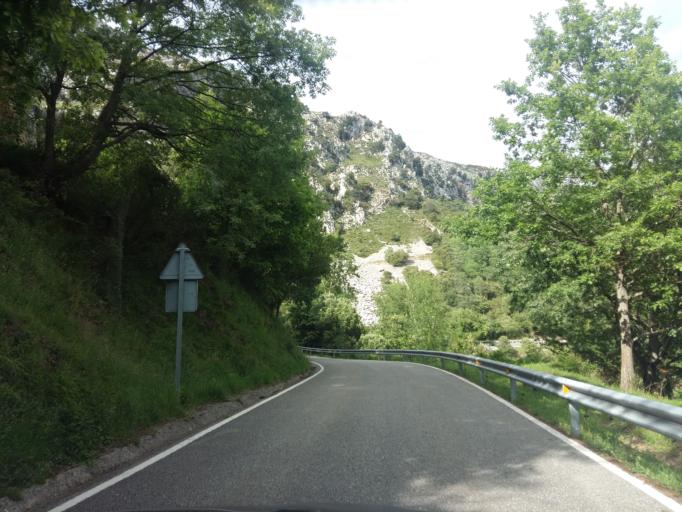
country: ES
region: Cantabria
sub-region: Provincia de Cantabria
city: Tresviso
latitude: 43.2538
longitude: -4.5986
